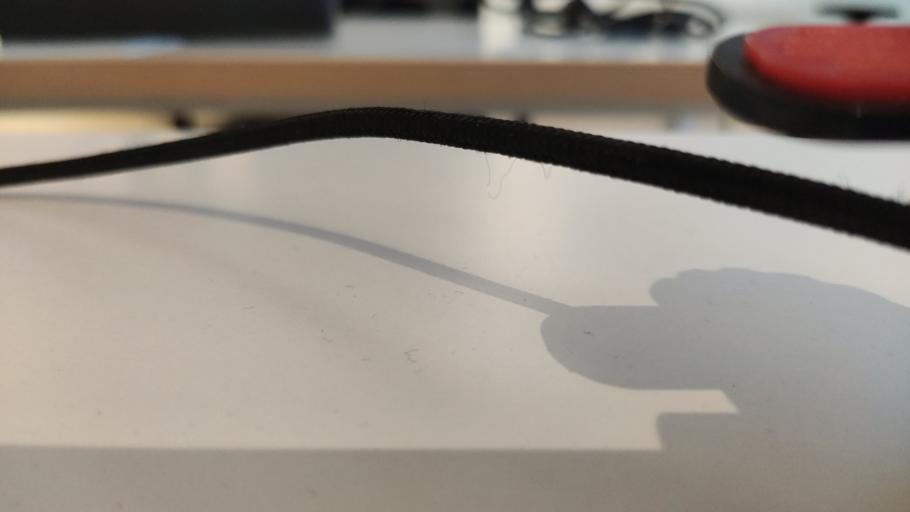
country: RU
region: Moskovskaya
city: Sychevo
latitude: 55.8460
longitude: 36.3436
